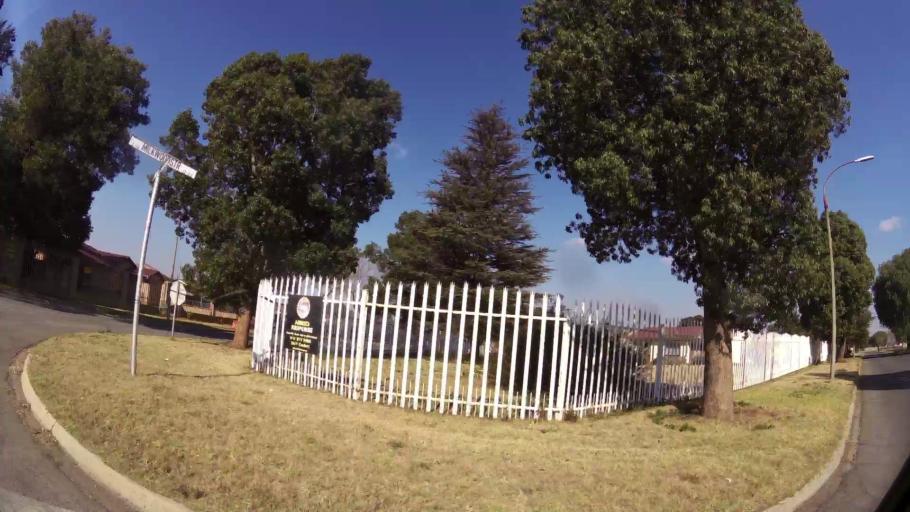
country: ZA
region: Gauteng
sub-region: Ekurhuleni Metropolitan Municipality
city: Boksburg
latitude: -26.2475
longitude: 28.2923
